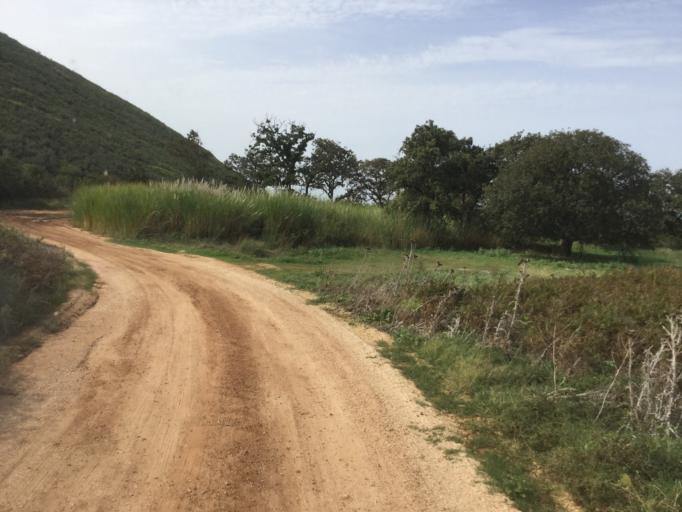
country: GR
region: West Greece
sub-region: Nomos Achaias
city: Lapas
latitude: 38.1755
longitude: 21.3694
